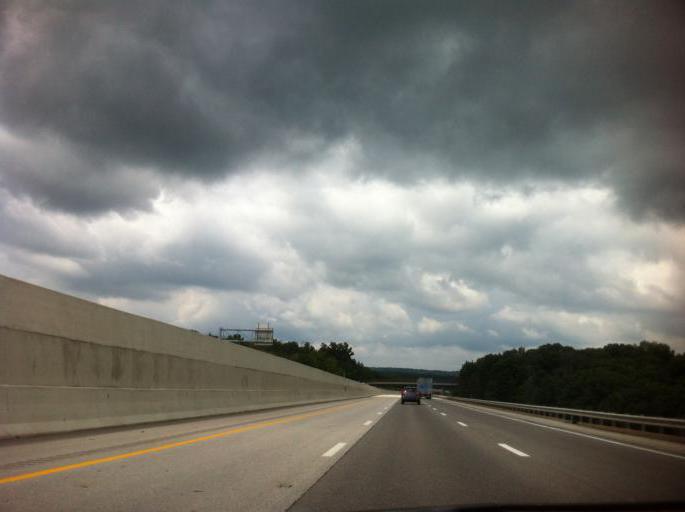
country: US
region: Ohio
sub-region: Summit County
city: Boston Heights
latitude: 41.2570
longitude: -81.5345
